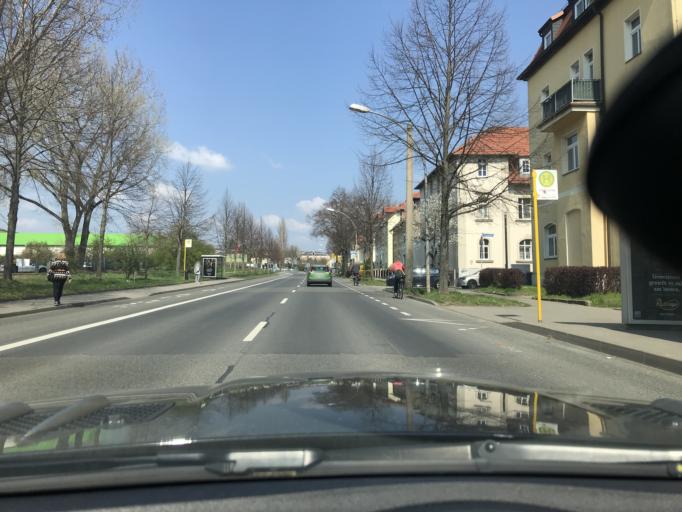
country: DE
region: Thuringia
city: Weimar
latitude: 50.9974
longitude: 11.3326
